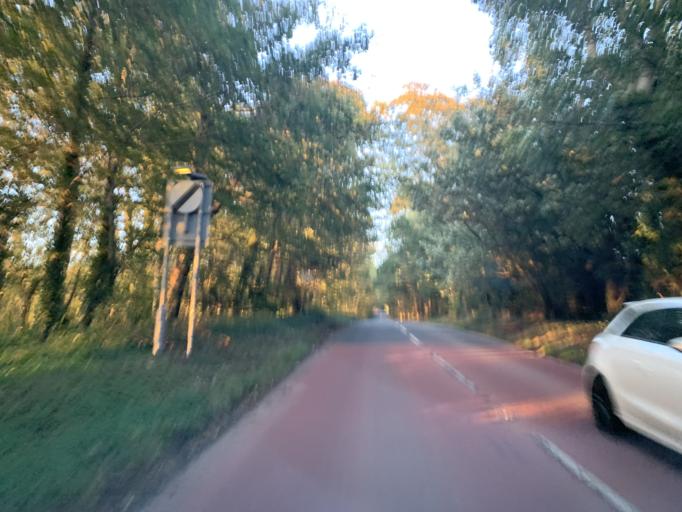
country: GB
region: England
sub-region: Wiltshire
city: Wilton
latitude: 51.0880
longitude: -1.8503
